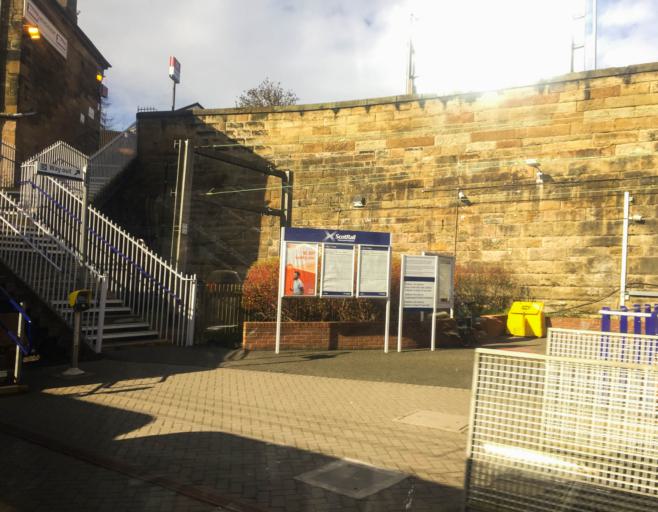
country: GB
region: Scotland
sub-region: East Dunbartonshire
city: Bishopbriggs
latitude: 55.8820
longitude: -4.2305
